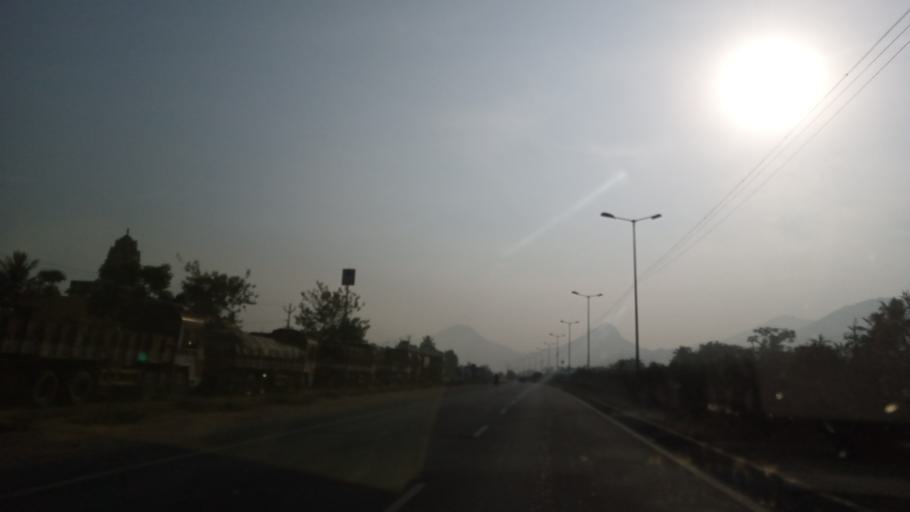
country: IN
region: Tamil Nadu
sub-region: Salem
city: Salem
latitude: 11.6262
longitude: 78.1570
